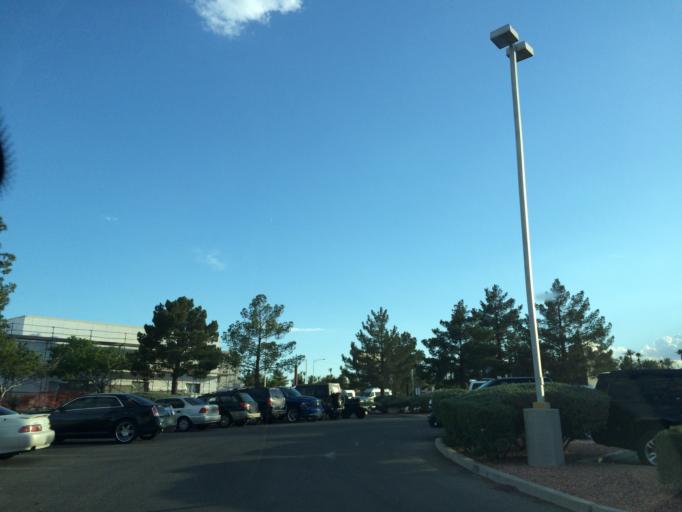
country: US
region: Nevada
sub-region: Clark County
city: Paradise
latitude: 36.0796
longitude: -115.1713
